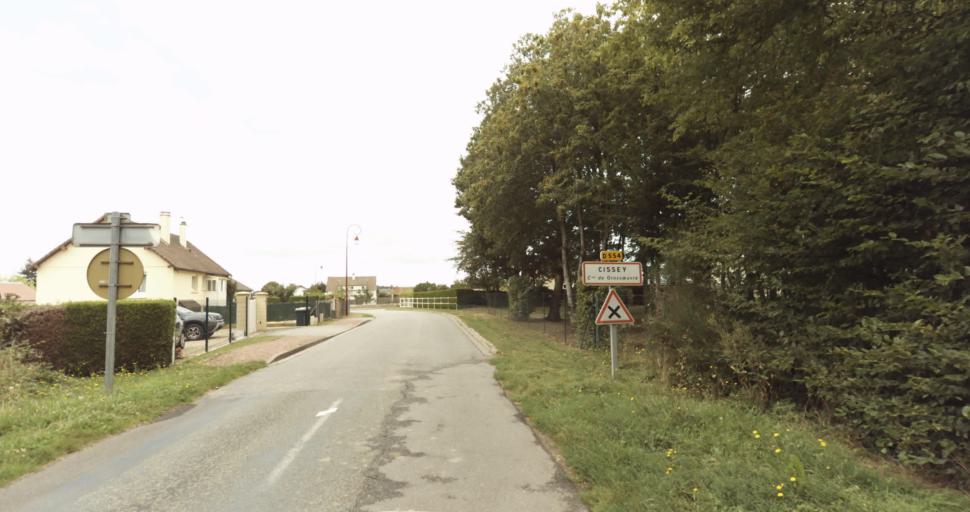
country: FR
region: Haute-Normandie
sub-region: Departement de l'Eure
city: Evreux
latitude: 48.9449
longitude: 1.1829
